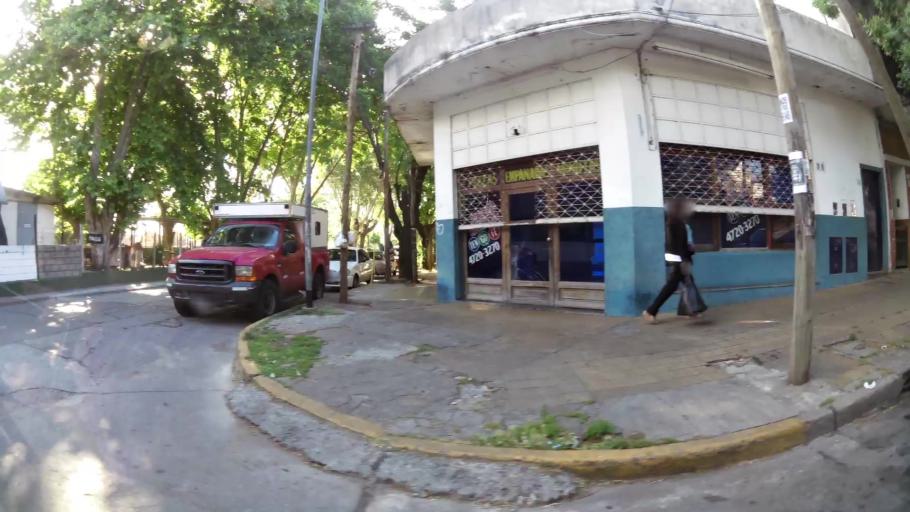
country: AR
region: Buenos Aires
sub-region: Partido de General San Martin
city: General San Martin
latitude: -34.5417
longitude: -58.5673
